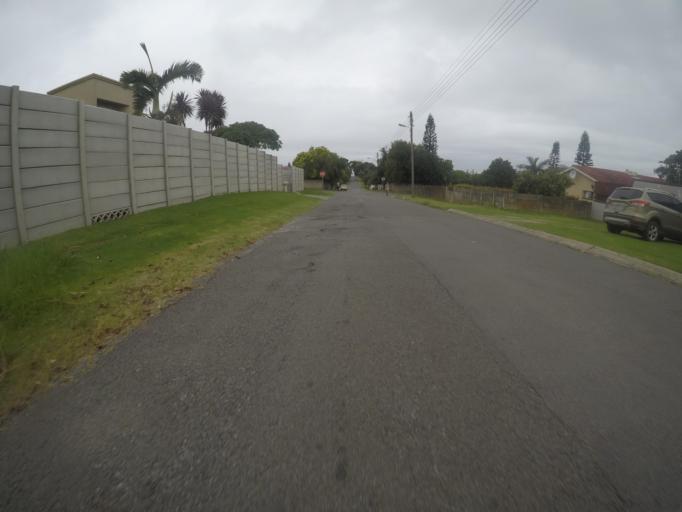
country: ZA
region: Eastern Cape
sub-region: Buffalo City Metropolitan Municipality
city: East London
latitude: -32.9399
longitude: 28.0040
